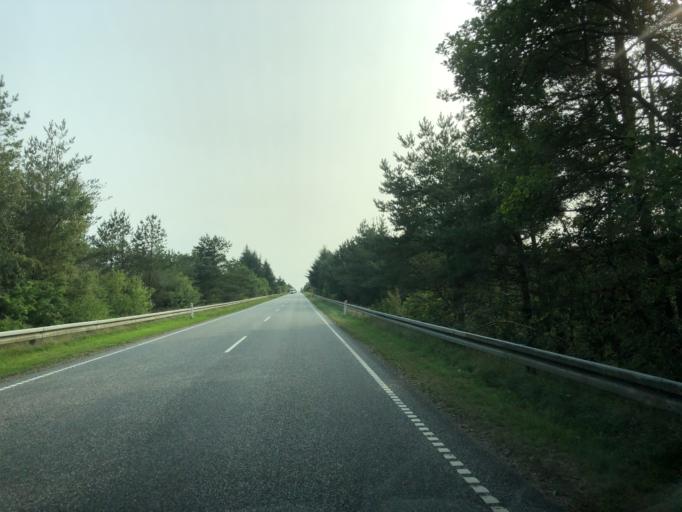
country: DK
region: Central Jutland
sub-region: Herning Kommune
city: Vildbjerg
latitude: 56.1757
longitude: 8.6930
